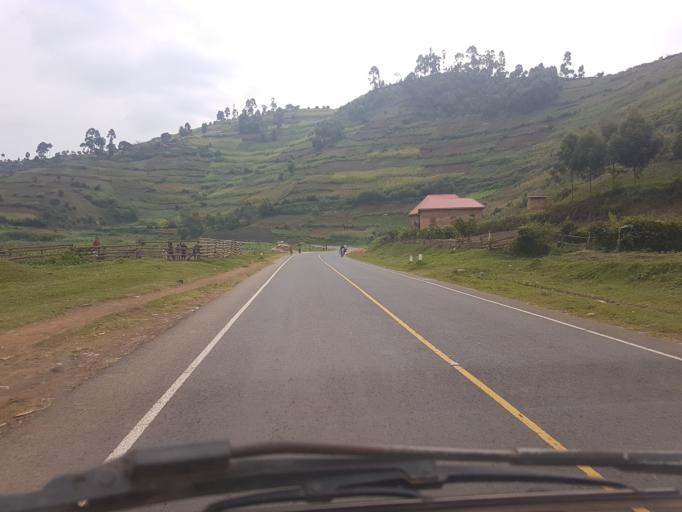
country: UG
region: Western Region
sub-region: Kisoro District
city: Kisoro
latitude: -1.2029
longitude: 29.8153
